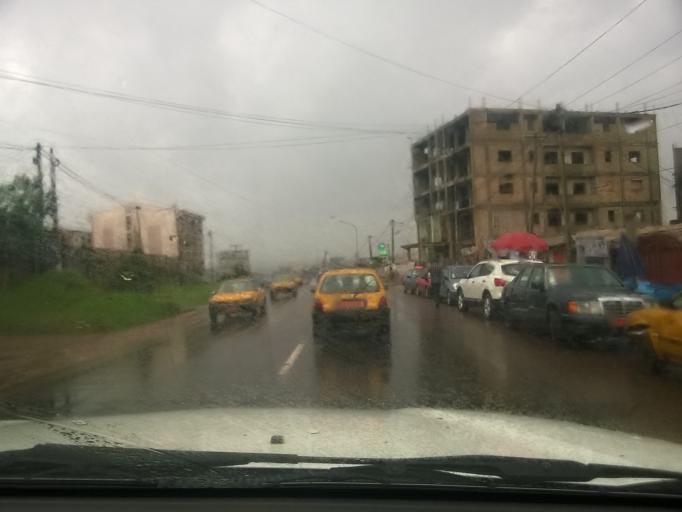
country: CM
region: Centre
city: Yaounde
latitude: 3.8817
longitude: 11.5388
